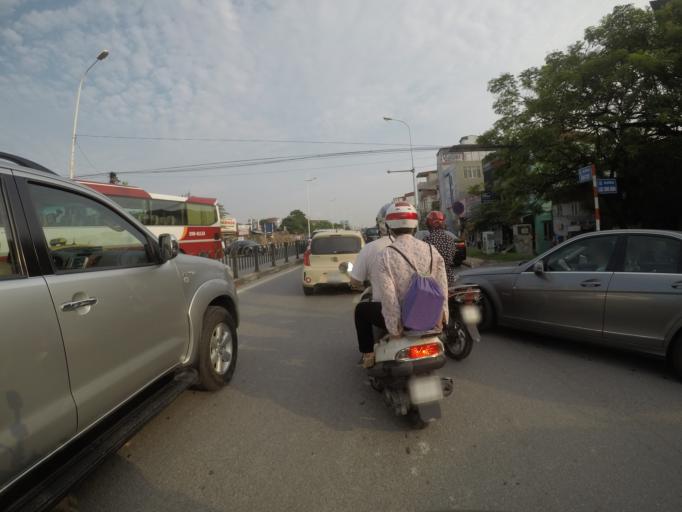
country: VN
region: Ha Noi
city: Tay Ho
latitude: 21.0809
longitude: 105.8182
